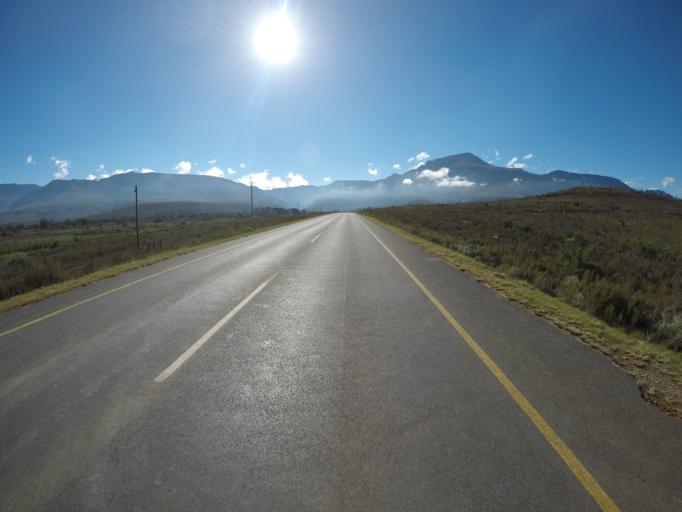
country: ZA
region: Western Cape
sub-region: Overberg District Municipality
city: Caledon
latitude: -34.0584
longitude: 19.5585
